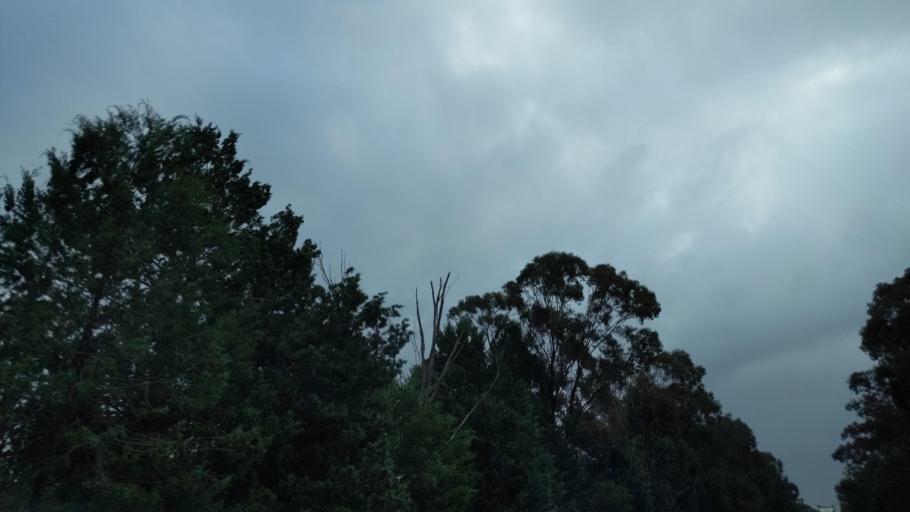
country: AU
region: New South Wales
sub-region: Coolamon
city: Coolamon
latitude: -34.9438
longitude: 147.3070
